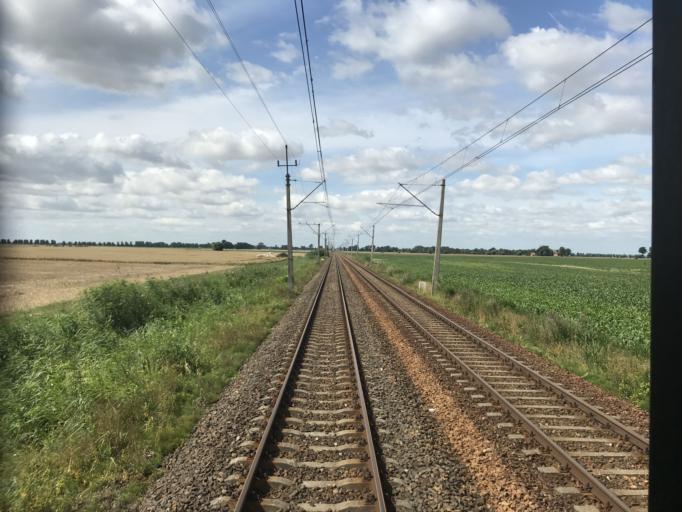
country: PL
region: Warmian-Masurian Voivodeship
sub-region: Powiat elblaski
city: Gronowo Elblaskie
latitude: 54.0773
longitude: 19.2738
